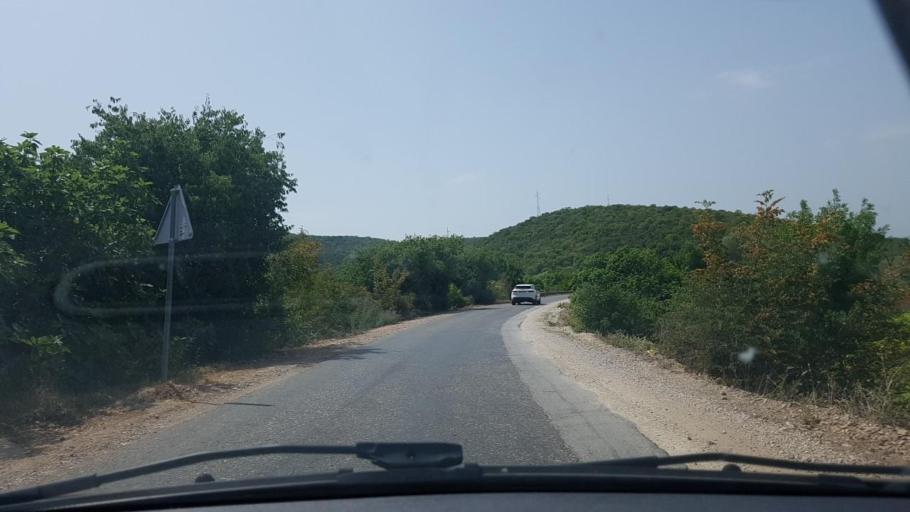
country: BA
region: Federation of Bosnia and Herzegovina
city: Tasovcici
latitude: 43.0223
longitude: 17.7604
